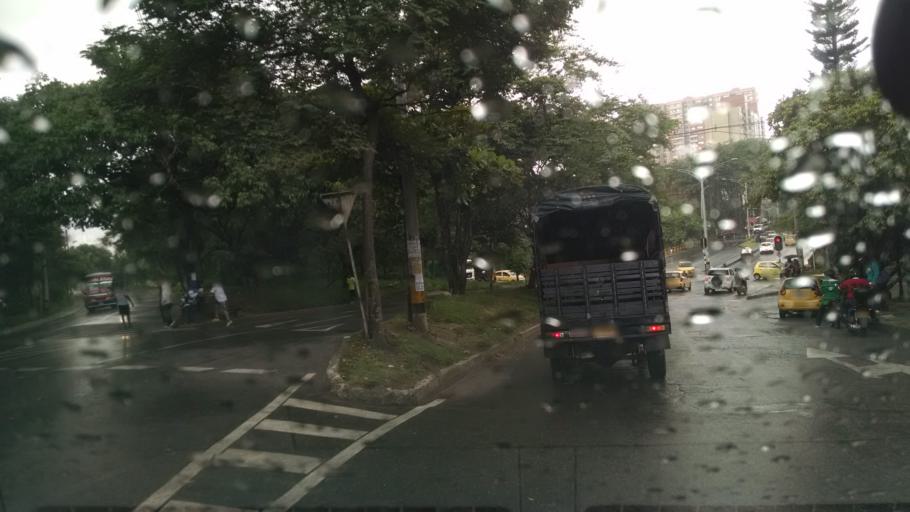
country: CO
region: Antioquia
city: Medellin
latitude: 6.2660
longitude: -75.5869
